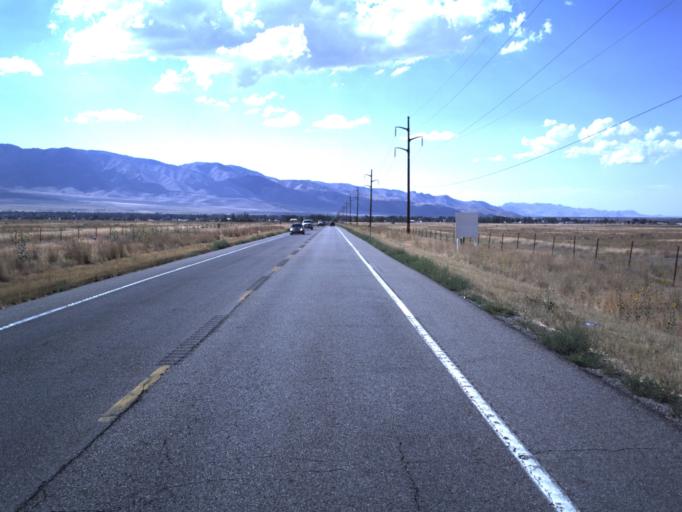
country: US
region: Utah
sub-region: Tooele County
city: Grantsville
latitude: 40.5797
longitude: -112.3963
